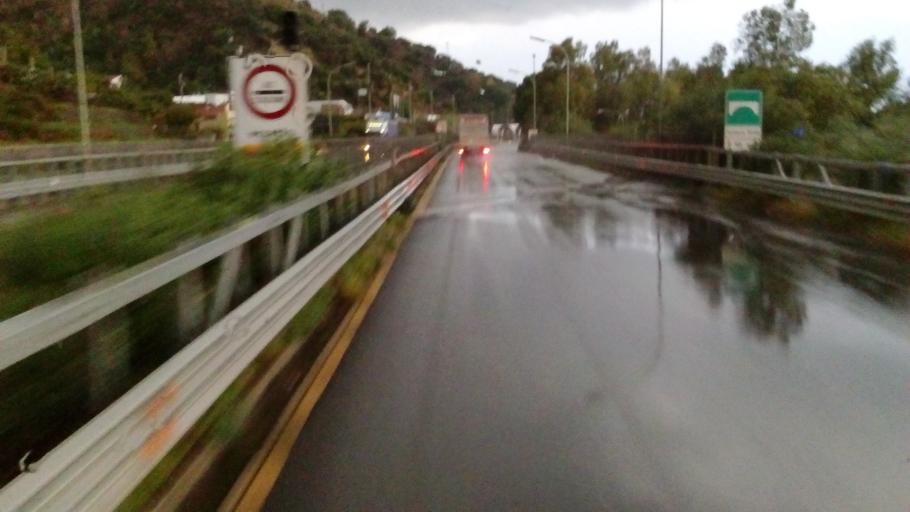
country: IT
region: Sicily
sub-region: Messina
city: Larderia
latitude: 38.1221
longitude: 15.5156
